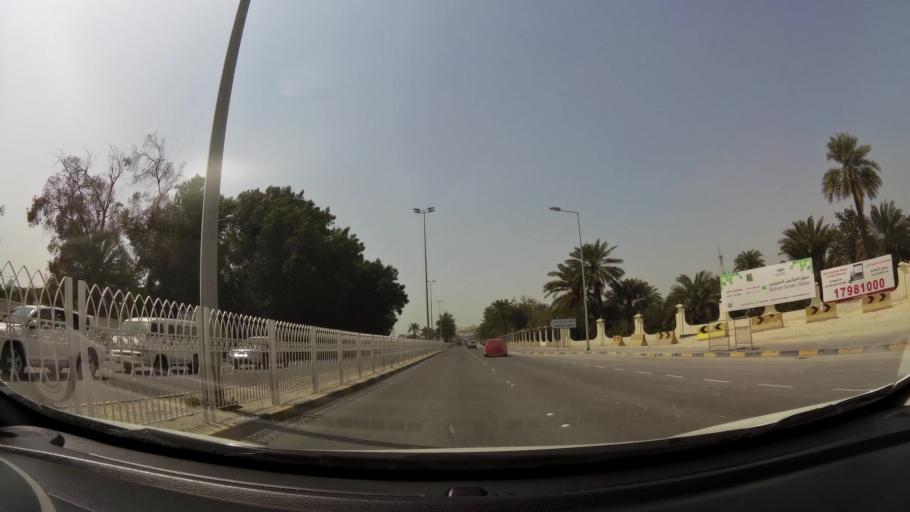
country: BH
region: Manama
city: Jidd Hafs
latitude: 26.2138
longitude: 50.4547
